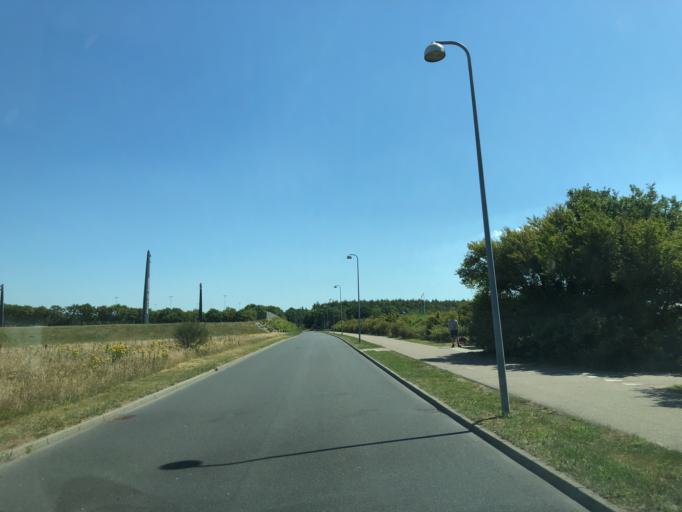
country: DK
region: Central Jutland
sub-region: Holstebro Kommune
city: Holstebro
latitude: 56.3614
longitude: 8.6790
